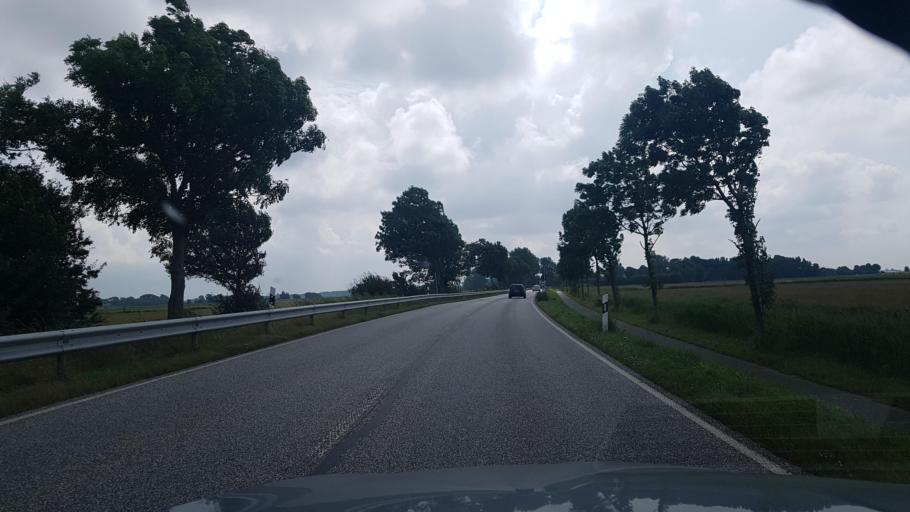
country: DE
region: Schleswig-Holstein
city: Kotzenbull
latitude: 54.3395
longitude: 8.8979
